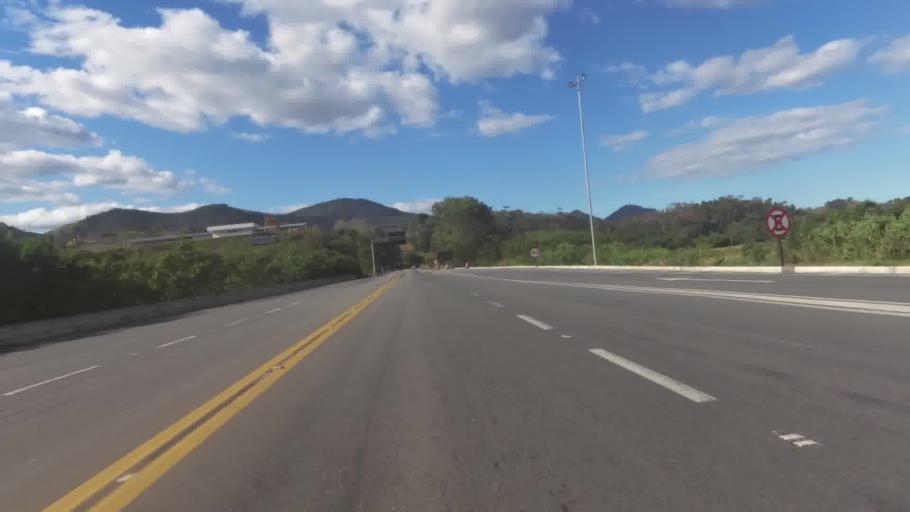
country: BR
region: Espirito Santo
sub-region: Rio Novo Do Sul
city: Rio Novo do Sul
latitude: -20.8773
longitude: -40.9648
